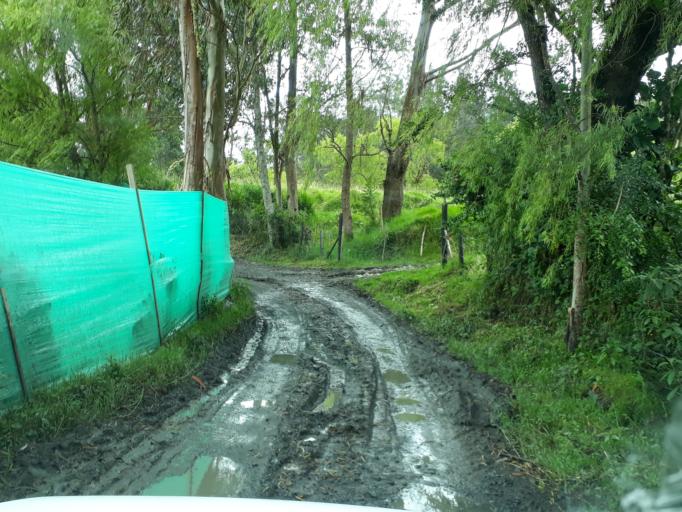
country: CO
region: Cundinamarca
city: Junin
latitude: 4.7591
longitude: -73.6252
